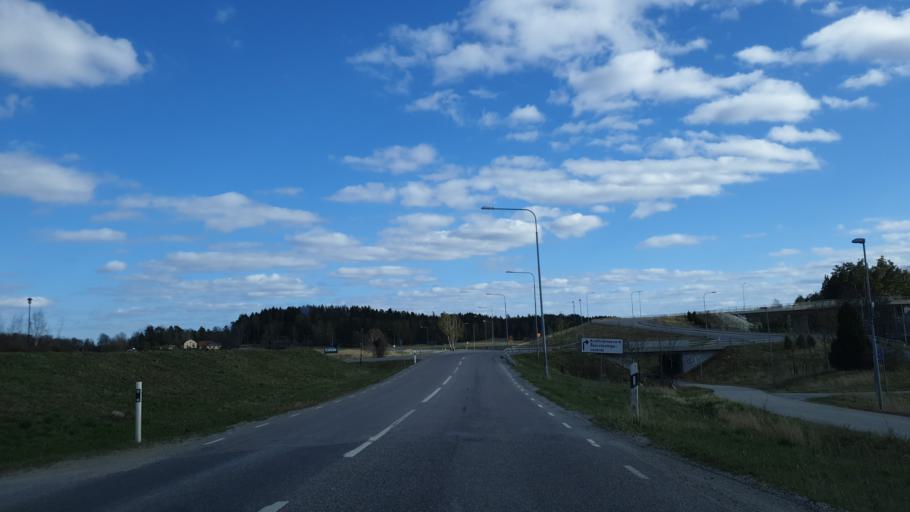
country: SE
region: Stockholm
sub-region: Sigtuna Kommun
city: Marsta
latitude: 59.6118
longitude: 17.8670
